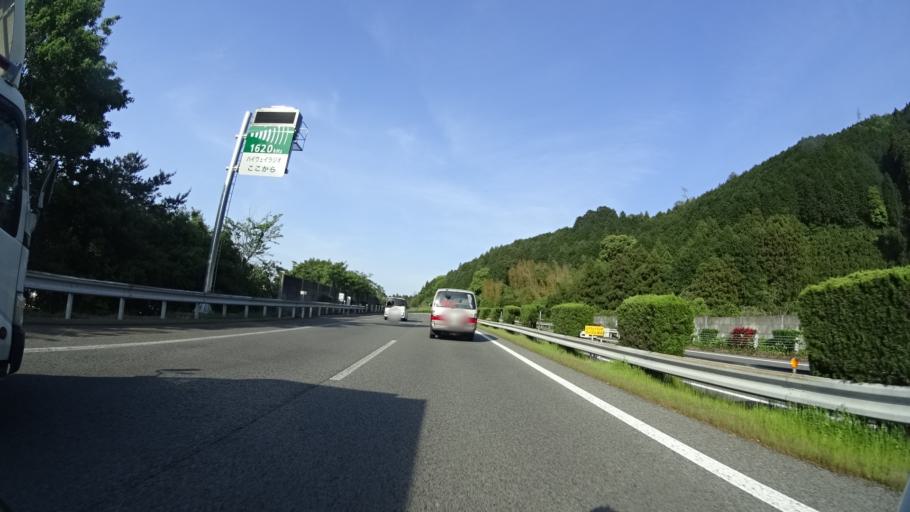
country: JP
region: Ehime
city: Niihama
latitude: 33.9360
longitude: 133.3769
